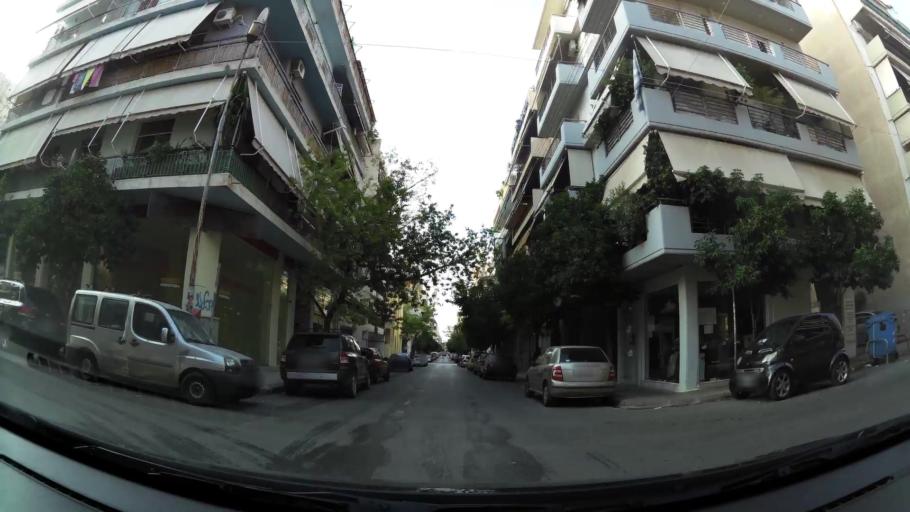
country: GR
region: Attica
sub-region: Nomarchia Athinas
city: Kallithea
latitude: 37.9567
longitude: 23.7083
